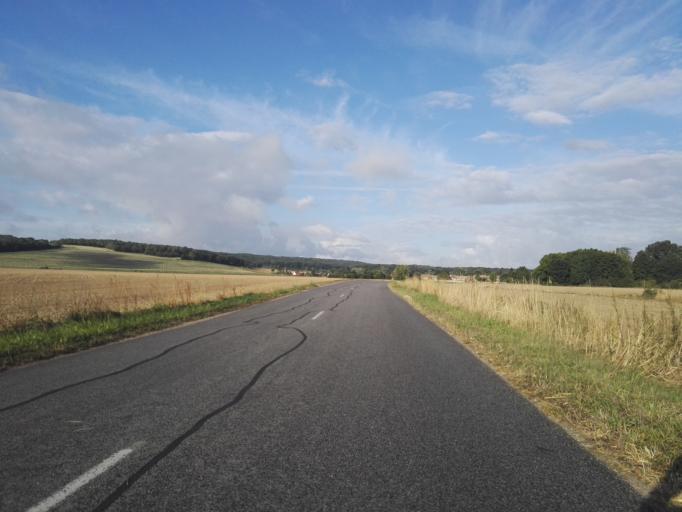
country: FR
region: Haute-Normandie
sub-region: Departement de l'Eure
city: Menilles
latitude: 49.0418
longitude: 1.3312
